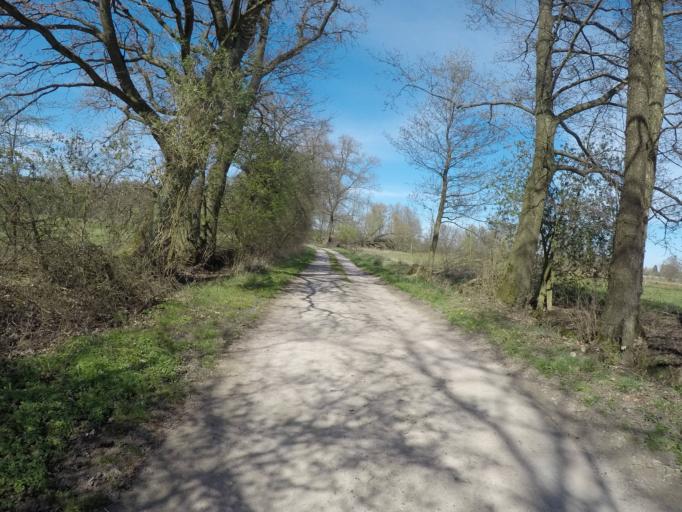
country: DE
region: Schleswig-Holstein
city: Jersbek
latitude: 53.7312
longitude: 10.1799
